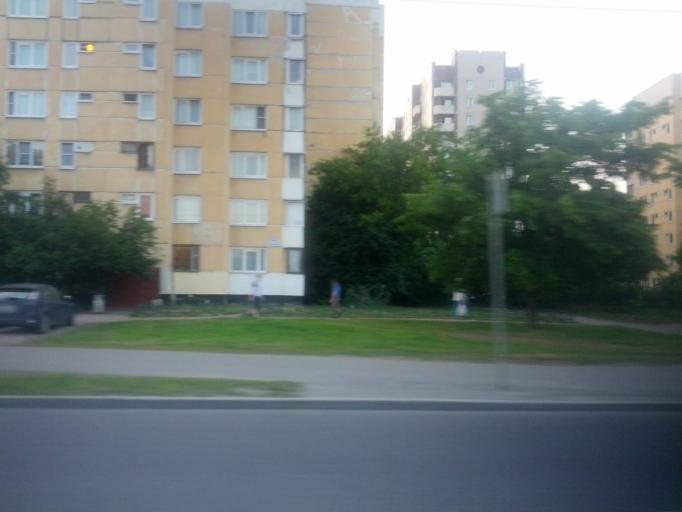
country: RU
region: St.-Petersburg
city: Staraya Derevnya
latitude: 59.9848
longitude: 30.2360
